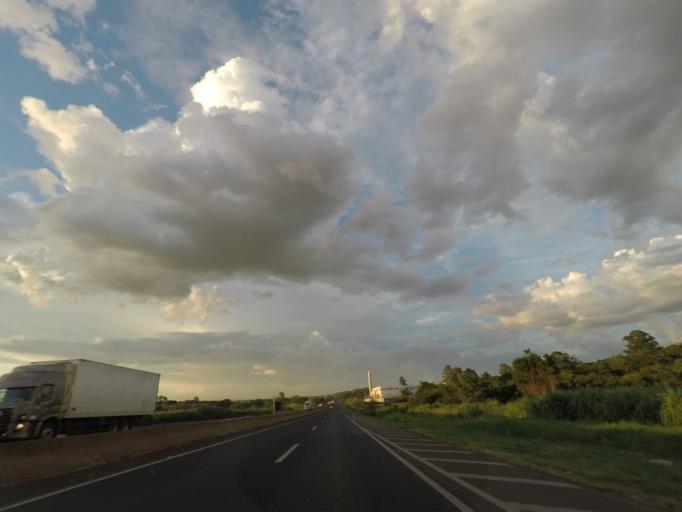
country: BR
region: Minas Gerais
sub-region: Uberaba
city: Uberaba
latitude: -19.7614
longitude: -47.9775
